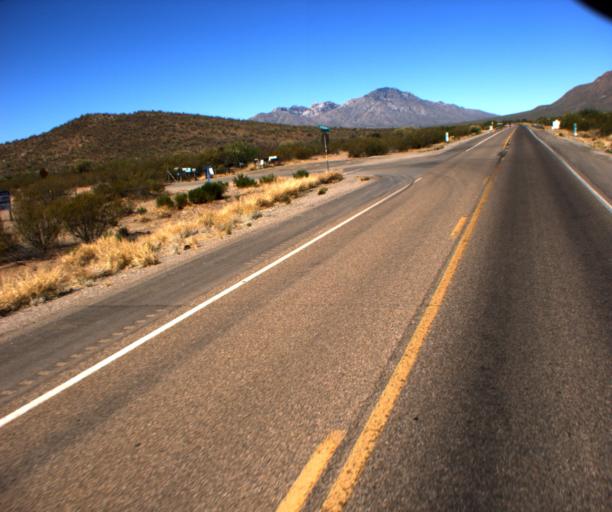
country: US
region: Arizona
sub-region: Pima County
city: Three Points
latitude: 32.0628
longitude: -111.3847
